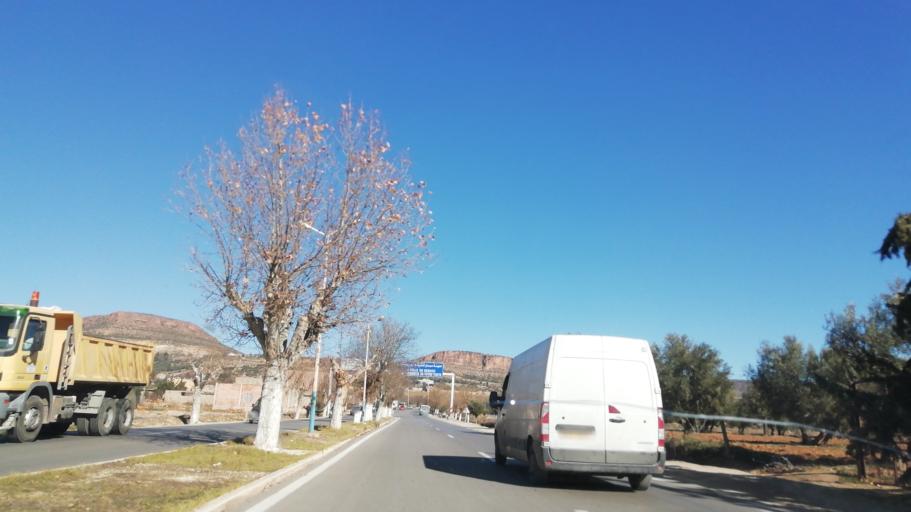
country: DZ
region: Tlemcen
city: Sebdou
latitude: 34.6708
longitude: -1.3187
